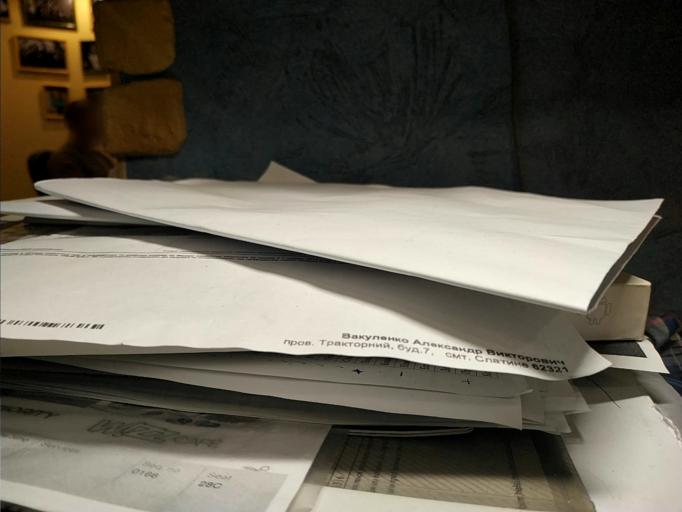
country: RU
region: Tverskaya
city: Zubtsov
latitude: 56.1065
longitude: 34.6516
